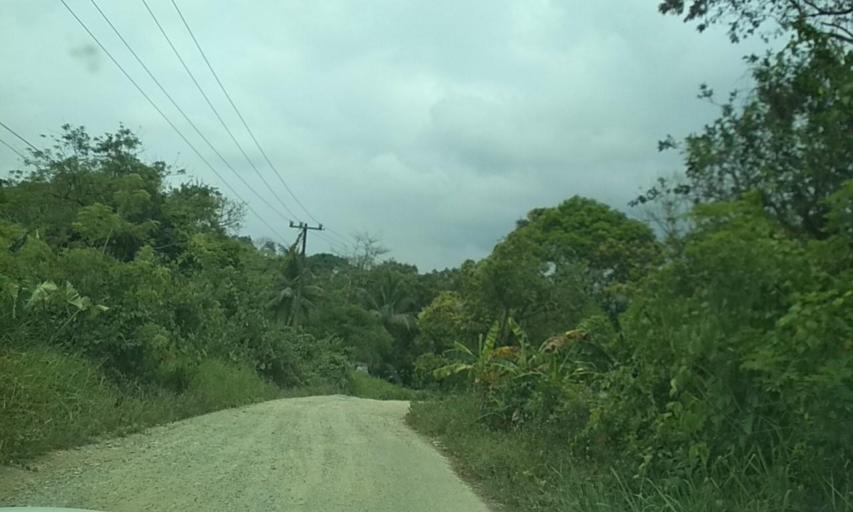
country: MX
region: Veracruz
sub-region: Uxpanapa
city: Poblado 10
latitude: 17.4977
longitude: -94.1431
